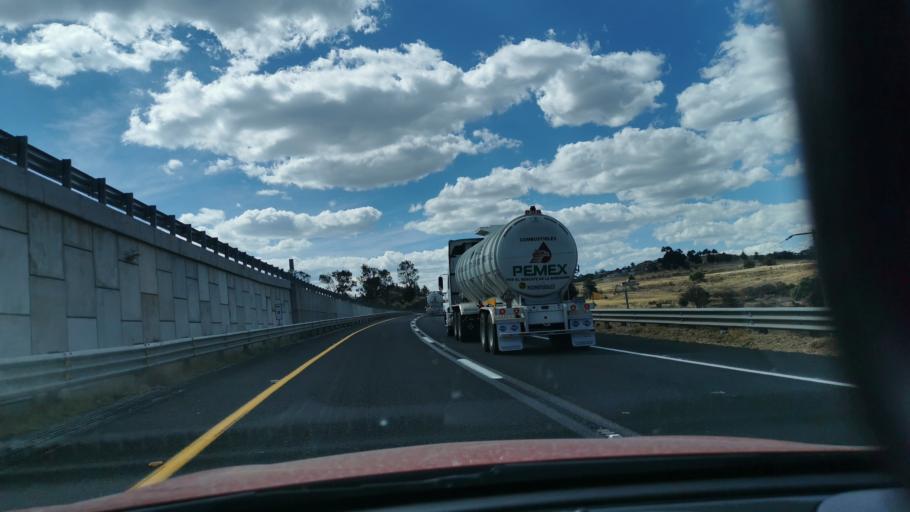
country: MX
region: Mexico
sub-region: Atlacomulco
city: San Bartolo Lanzados
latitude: 19.8818
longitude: -99.8571
